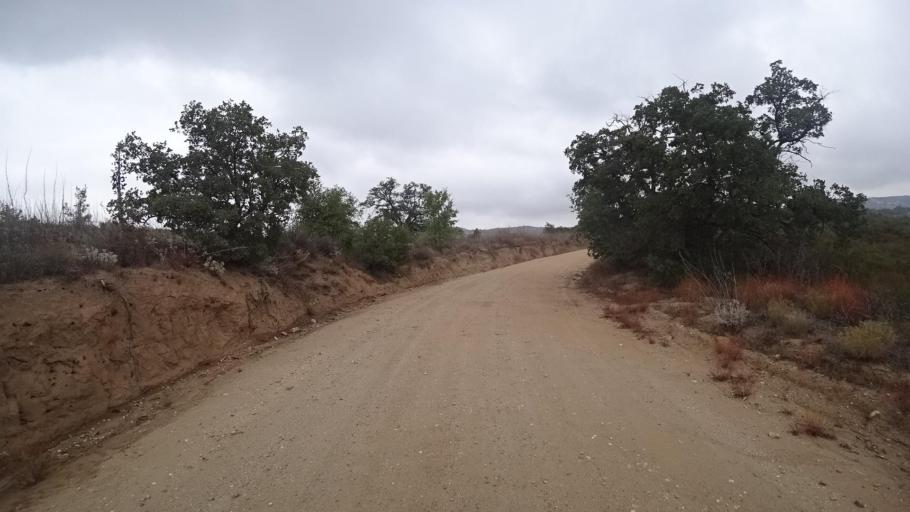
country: US
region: California
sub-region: San Diego County
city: San Diego Country Estates
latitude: 32.9843
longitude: -116.6732
